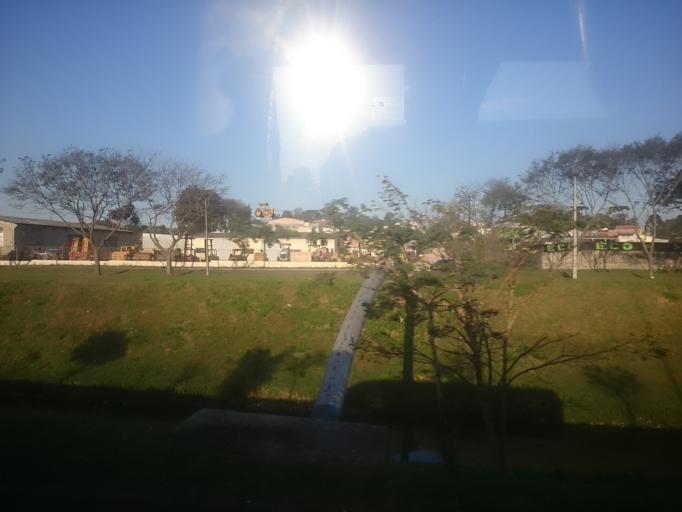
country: BR
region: Parana
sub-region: Curitiba
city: Curitiba
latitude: -25.4632
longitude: -49.2511
